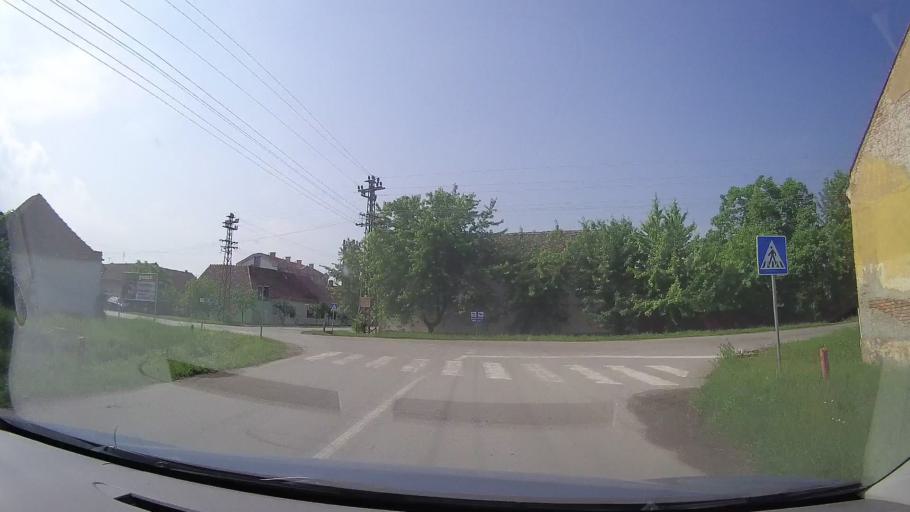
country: RS
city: Jasa Tomic
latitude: 45.4483
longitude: 20.8551
